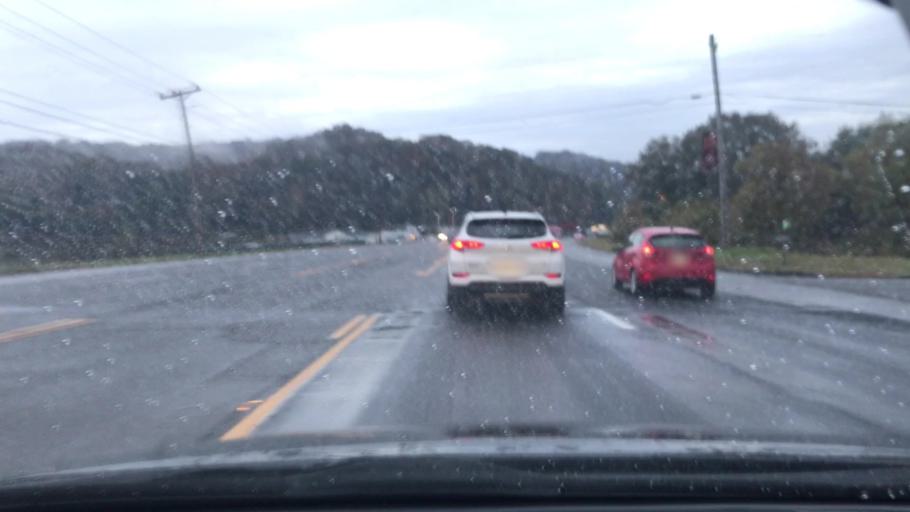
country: US
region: Tennessee
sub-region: Cheatham County
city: Ashland City
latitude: 36.2605
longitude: -87.0475
